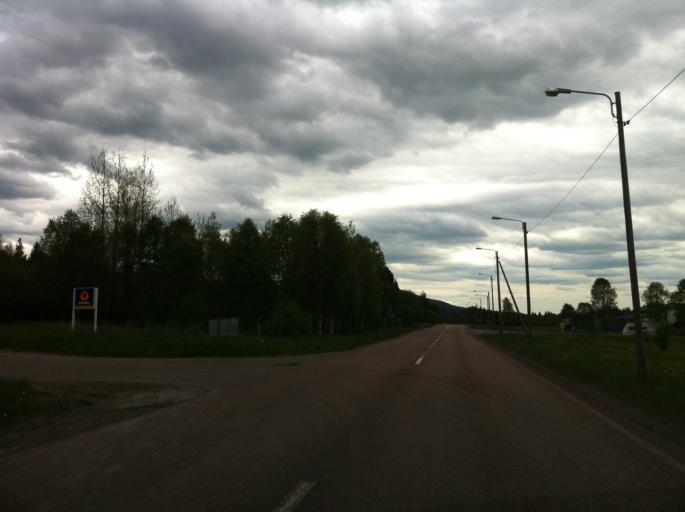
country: SE
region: Dalarna
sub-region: Malung-Saelens kommun
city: Malung
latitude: 61.0783
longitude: 13.3256
